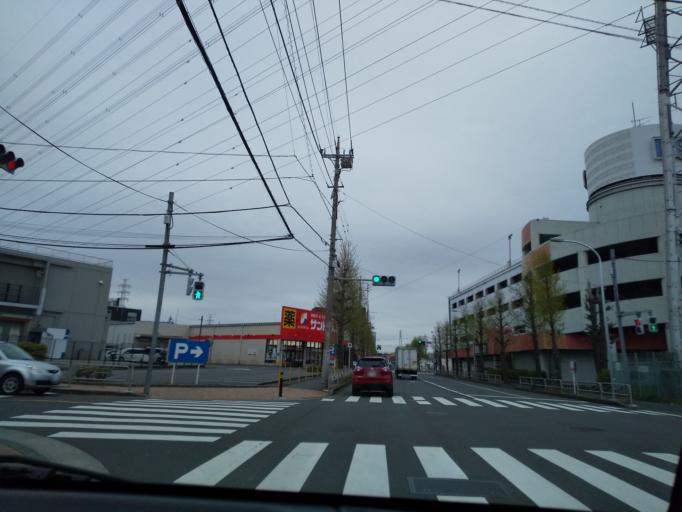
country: JP
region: Tokyo
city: Hino
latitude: 35.6641
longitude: 139.3676
